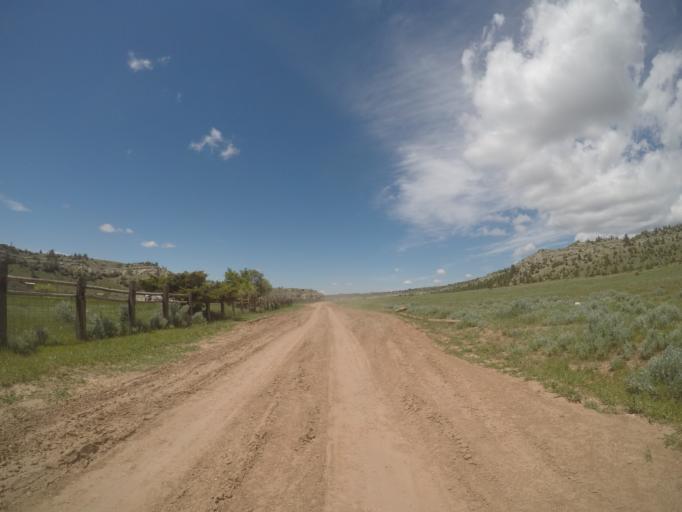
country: US
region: Montana
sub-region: Yellowstone County
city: Laurel
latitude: 45.2388
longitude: -108.6302
